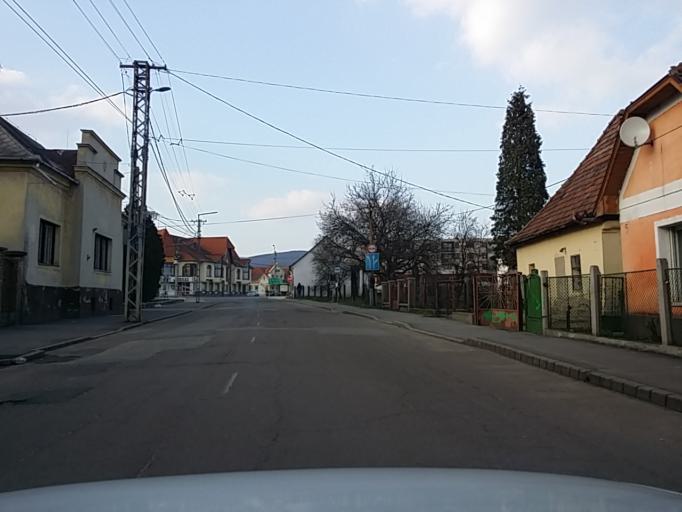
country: HU
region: Borsod-Abauj-Zemplen
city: Putnok
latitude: 48.2931
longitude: 20.4371
